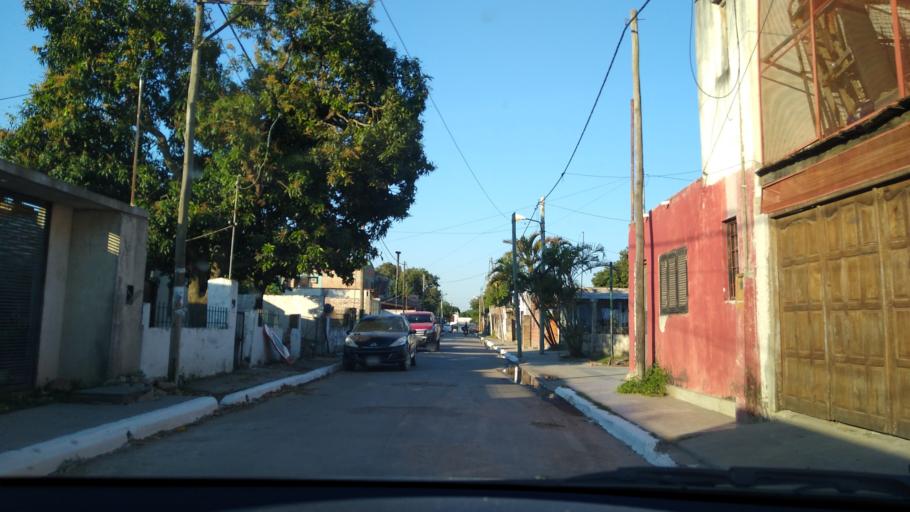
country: AR
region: Chaco
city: Puerto Vilelas
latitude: -27.5122
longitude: -58.9414
